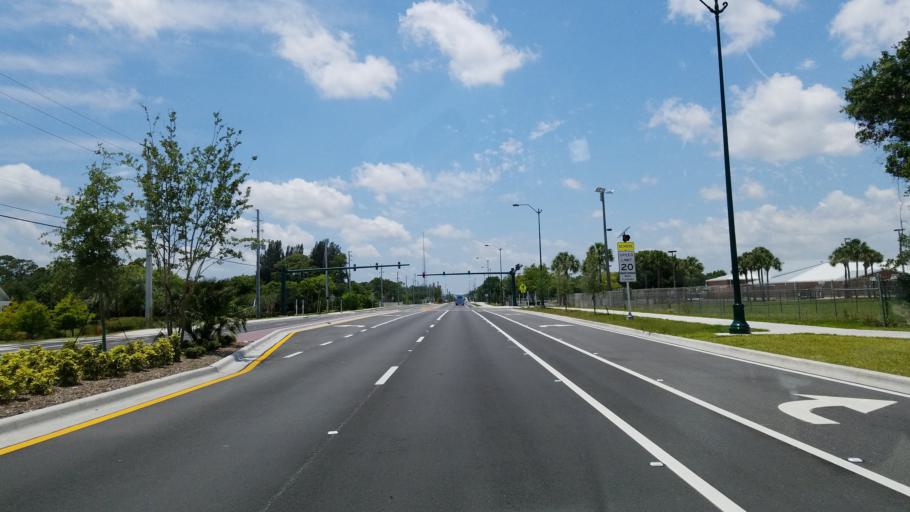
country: US
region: Florida
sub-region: Martin County
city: Palm City
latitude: 27.1614
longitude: -80.2896
